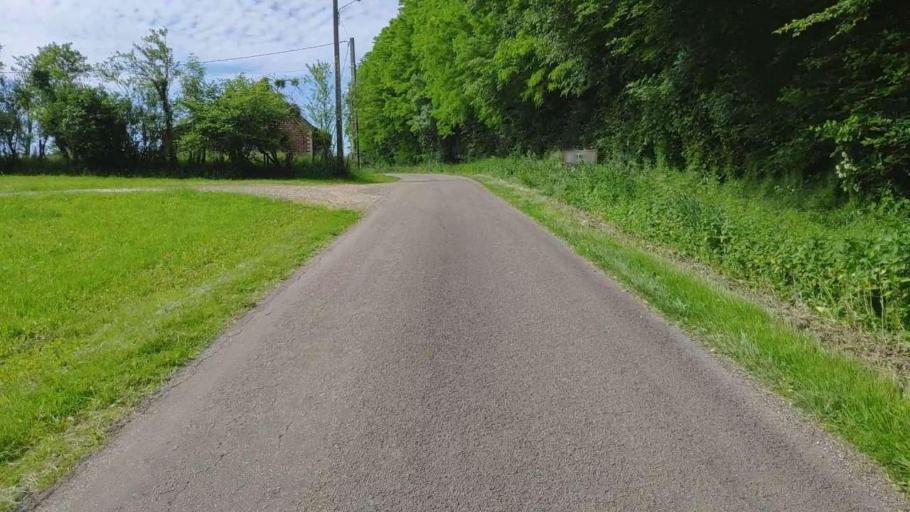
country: FR
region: Franche-Comte
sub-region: Departement du Jura
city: Bletterans
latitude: 46.7134
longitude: 5.4416
